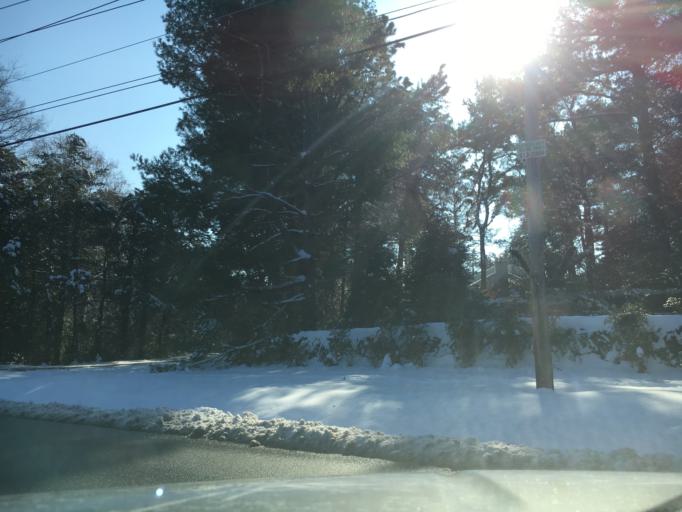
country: US
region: Virginia
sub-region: Henrico County
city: Tuckahoe
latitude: 37.5730
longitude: -77.5505
